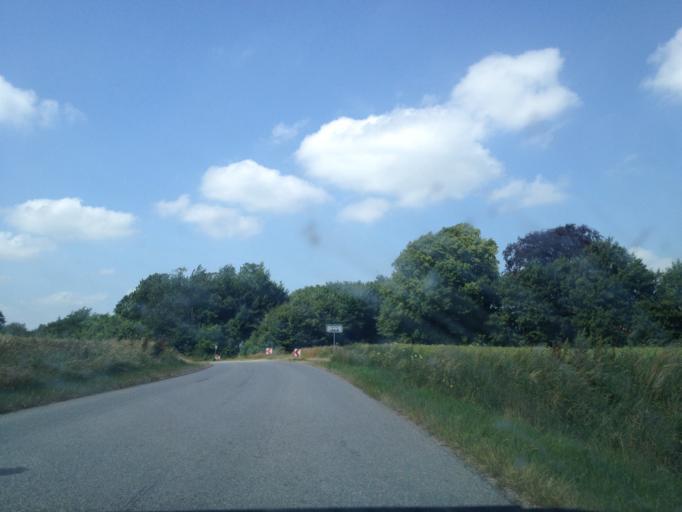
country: DK
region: South Denmark
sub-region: Kolding Kommune
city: Vamdrup
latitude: 55.3826
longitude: 9.2736
